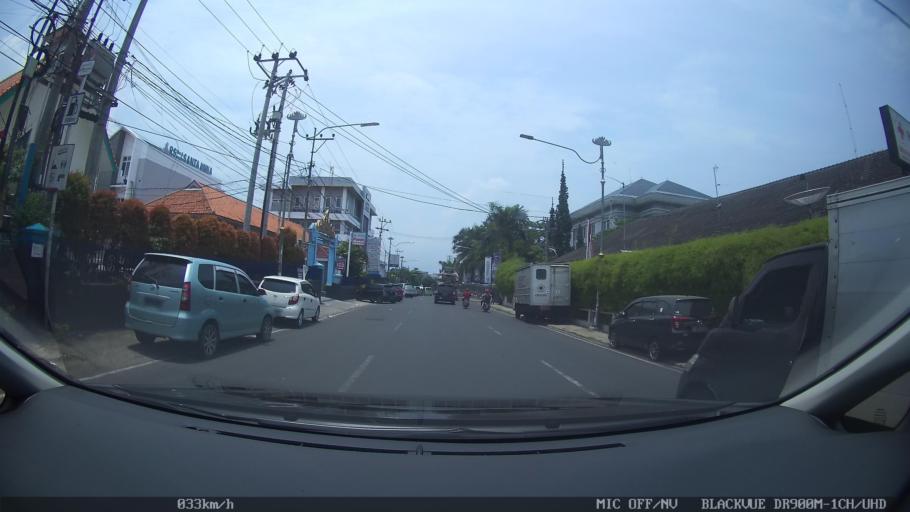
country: ID
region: Lampung
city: Bandarlampung
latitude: -5.4424
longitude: 105.2671
